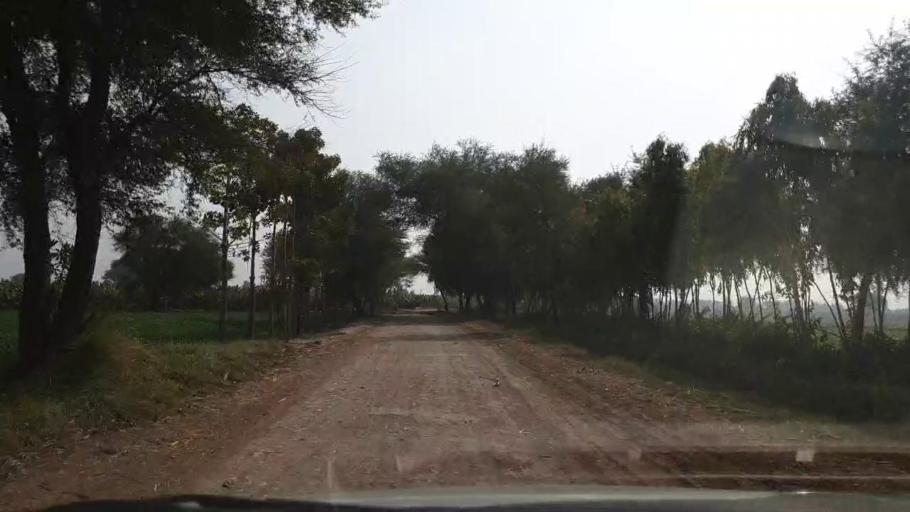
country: PK
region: Sindh
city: Matiari
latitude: 25.6561
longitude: 68.5499
